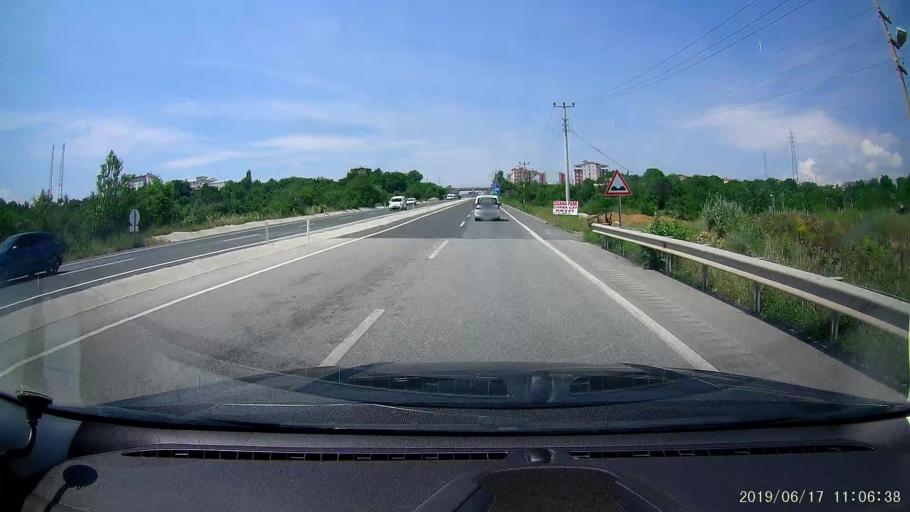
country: TR
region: Kastamonu
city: Tosya
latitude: 41.0112
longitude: 34.0644
